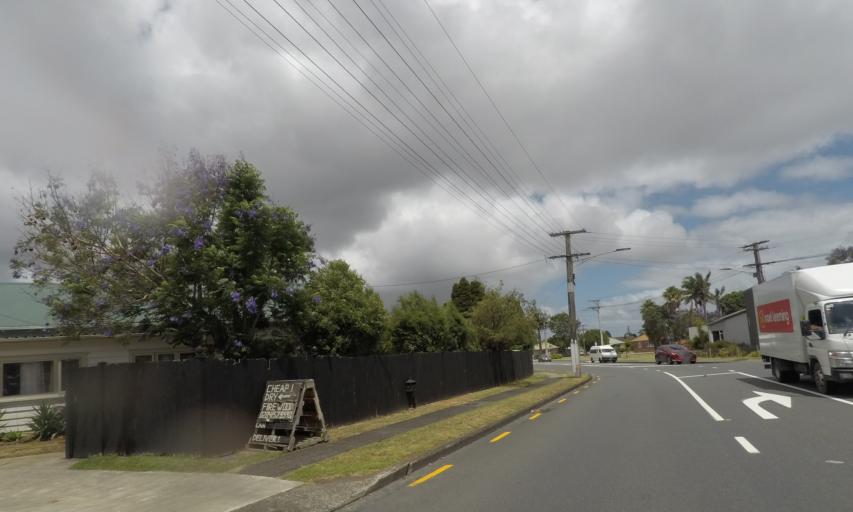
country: NZ
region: Northland
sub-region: Whangarei
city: Whangarei
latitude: -35.7023
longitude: 174.3154
